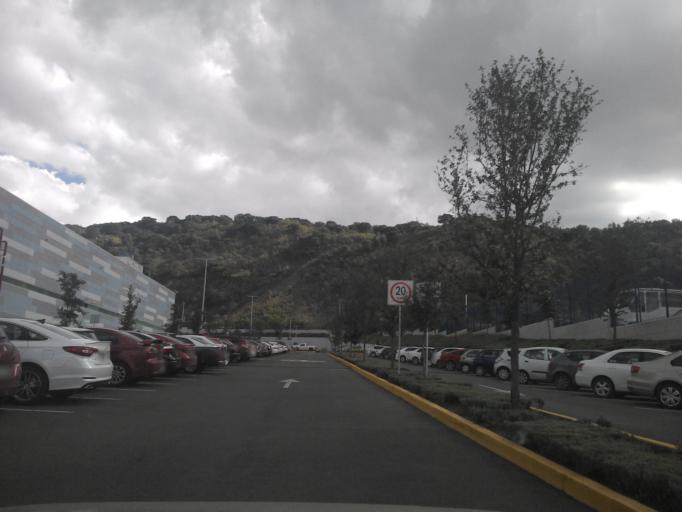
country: MX
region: Jalisco
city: Guadalajara
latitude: 20.6676
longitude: -103.4635
